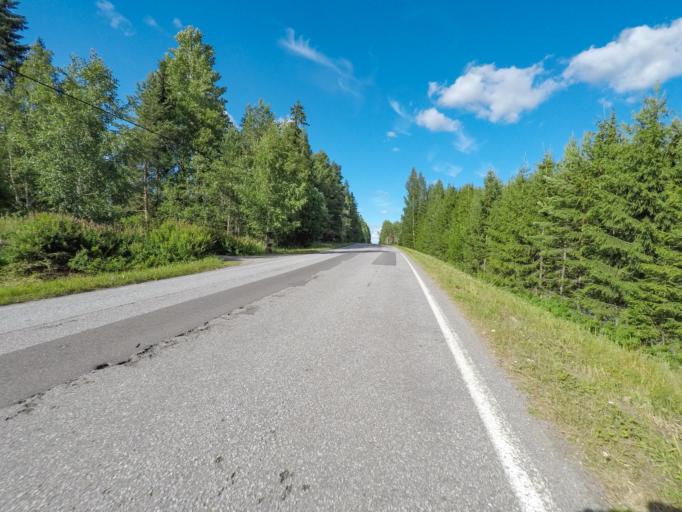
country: FI
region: South Karelia
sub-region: Imatra
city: Imatra
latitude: 61.1307
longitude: 28.7237
